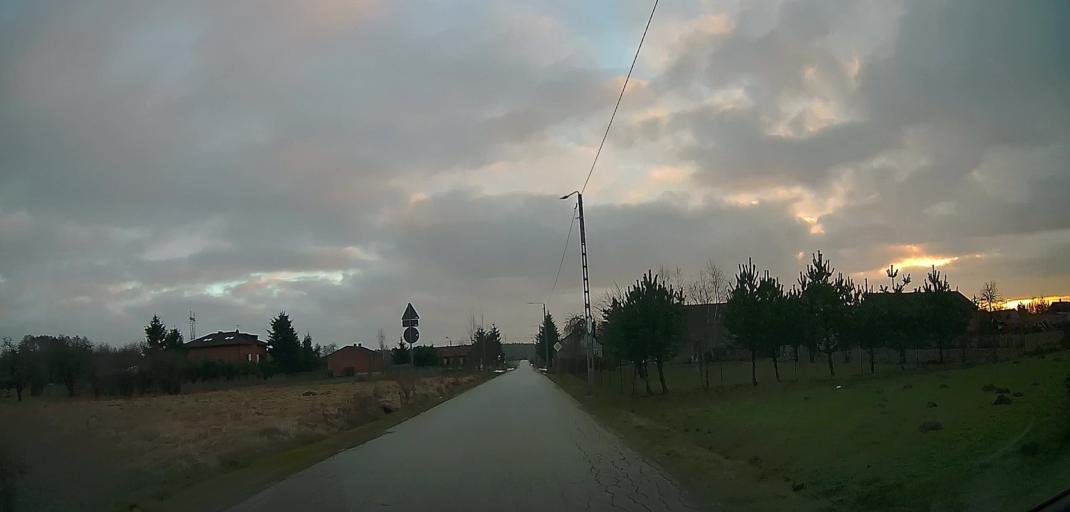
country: PL
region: Masovian Voivodeship
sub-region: Powiat radomski
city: Jedlinsk
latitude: 51.4583
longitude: 21.1236
